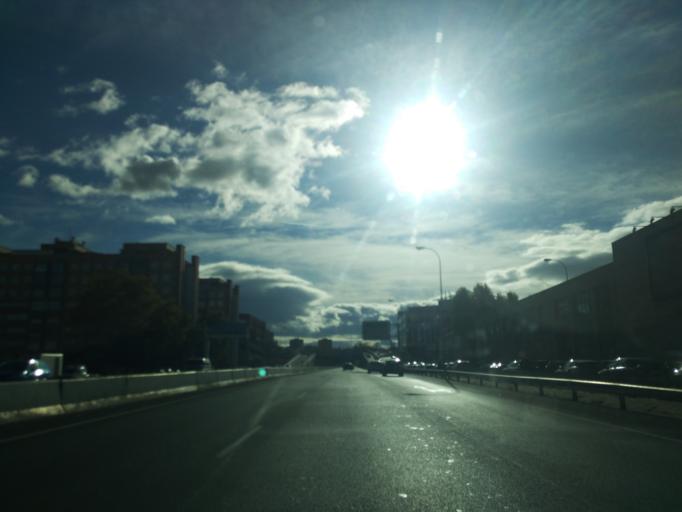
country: ES
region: Madrid
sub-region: Provincia de Madrid
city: Usera
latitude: 40.3792
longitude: -3.6926
